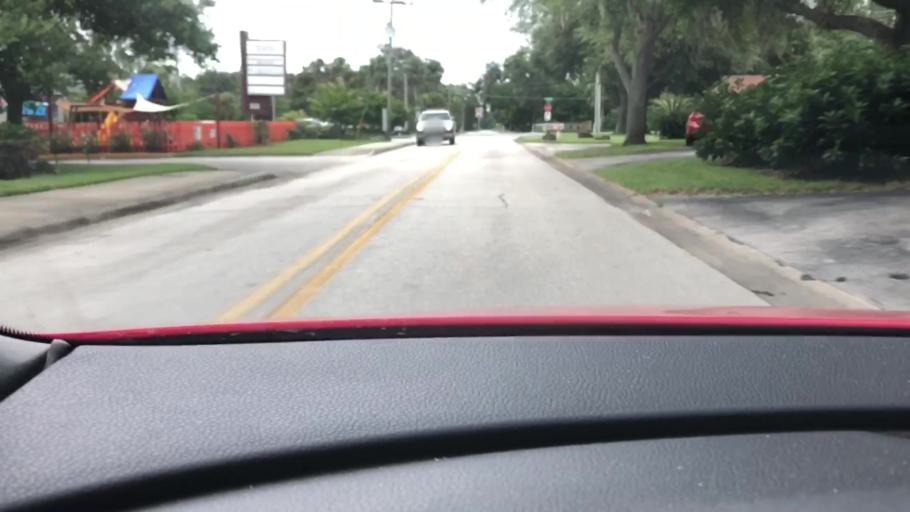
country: US
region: Florida
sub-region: Volusia County
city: Ormond Beach
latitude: 29.2798
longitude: -81.0809
